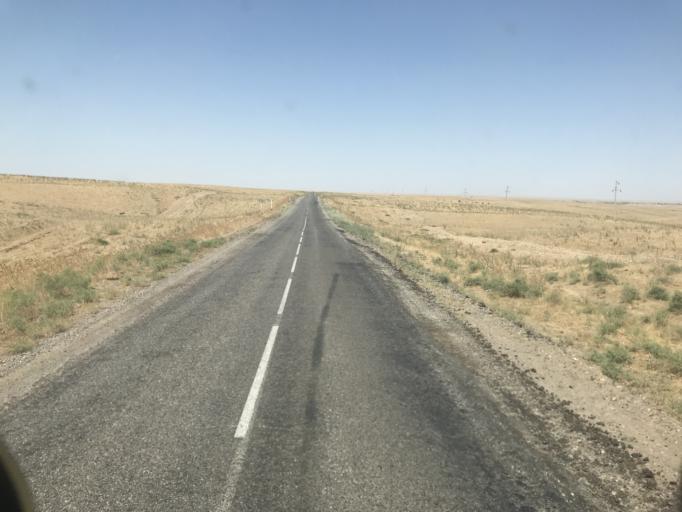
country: UZ
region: Toshkent
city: Chinoz
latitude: 41.1594
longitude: 68.6612
